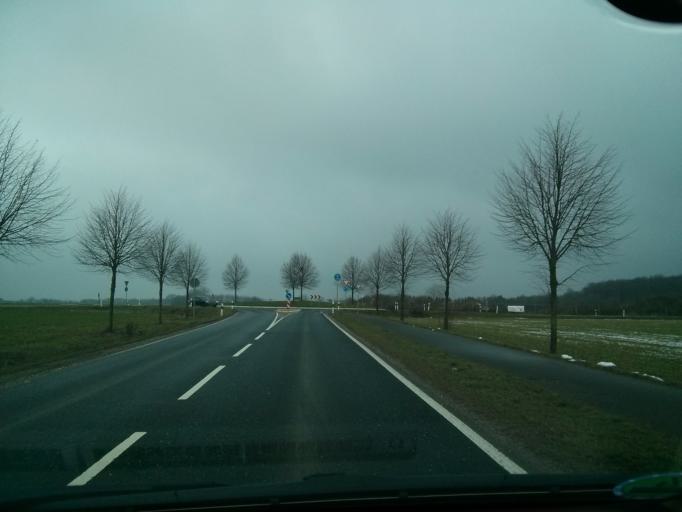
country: DE
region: North Rhine-Westphalia
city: Meckenheim
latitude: 50.6561
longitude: 7.0030
